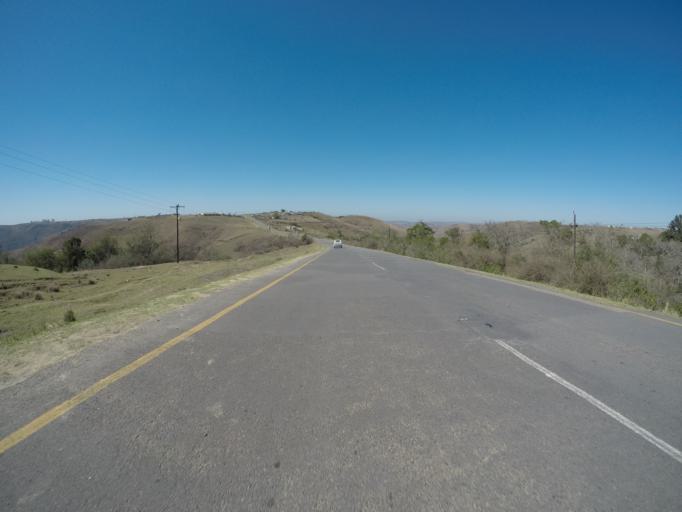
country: ZA
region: Eastern Cape
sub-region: OR Tambo District Municipality
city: Mthatha
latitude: -31.9008
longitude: 28.9460
